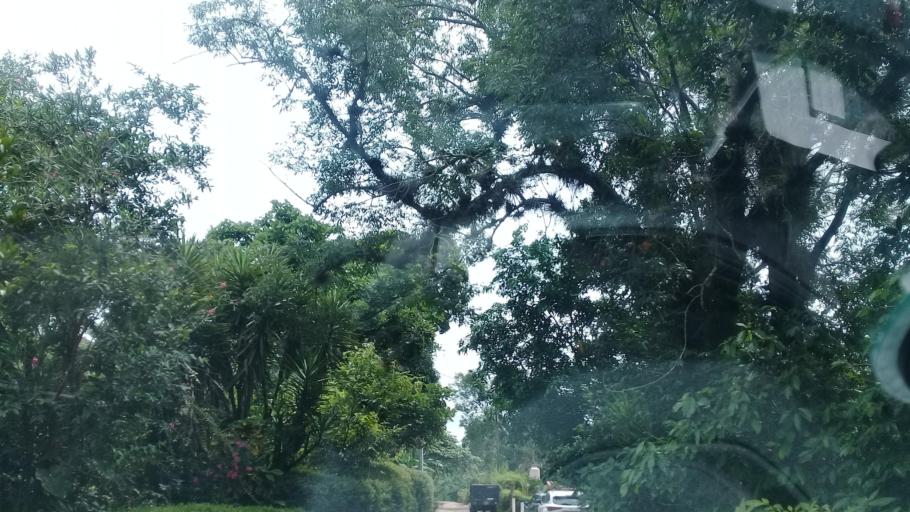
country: MX
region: Veracruz
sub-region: Xalapa
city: Colonia Santa Barbara
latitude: 19.4966
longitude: -96.8726
